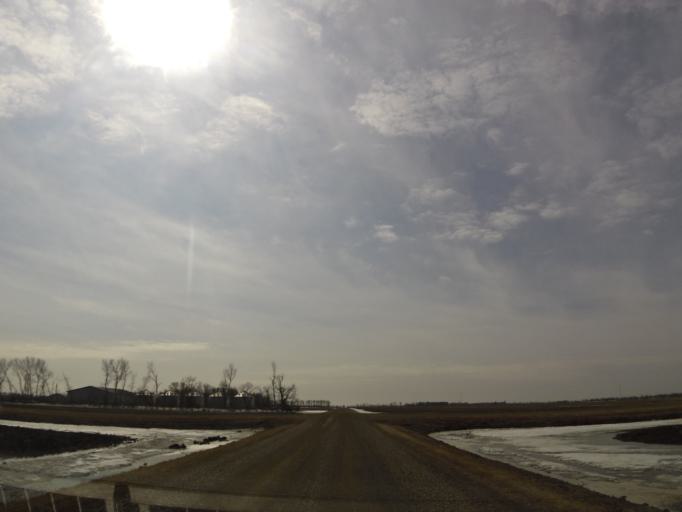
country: US
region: North Dakota
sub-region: Walsh County
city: Grafton
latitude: 48.3248
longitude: -97.2112
